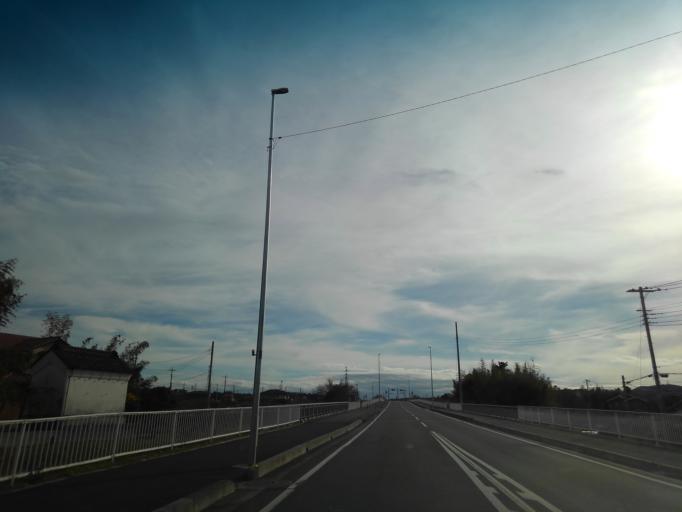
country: JP
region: Saitama
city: Morohongo
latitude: 35.9370
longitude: 139.3173
